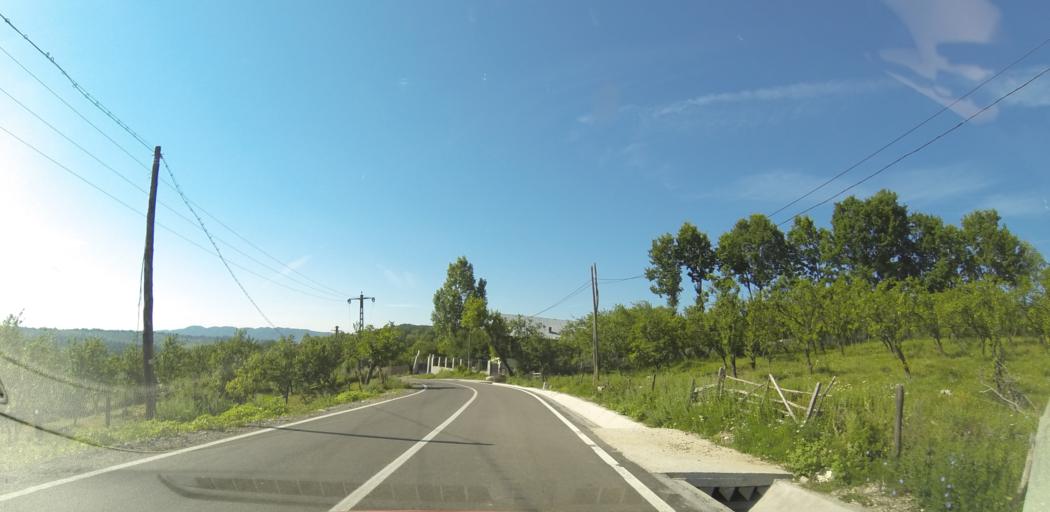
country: RO
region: Valcea
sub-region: Comuna Vaideeni
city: Vaideeni
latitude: 45.1661
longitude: 23.8885
